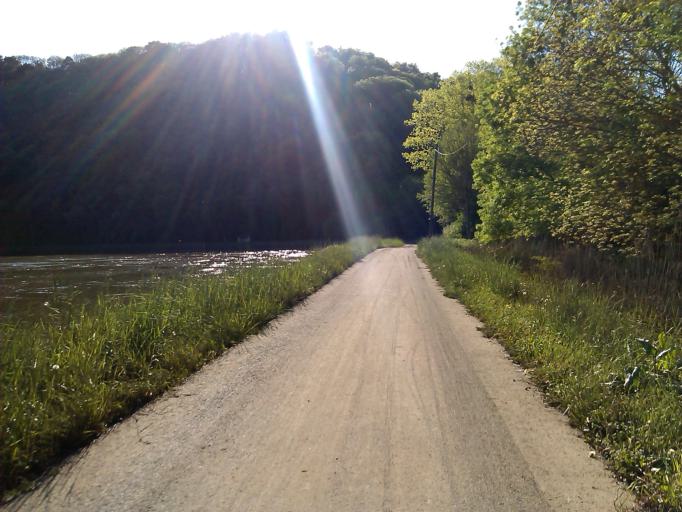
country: FR
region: Franche-Comte
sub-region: Departement du Doubs
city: Clerval
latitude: 47.4416
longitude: 6.5357
